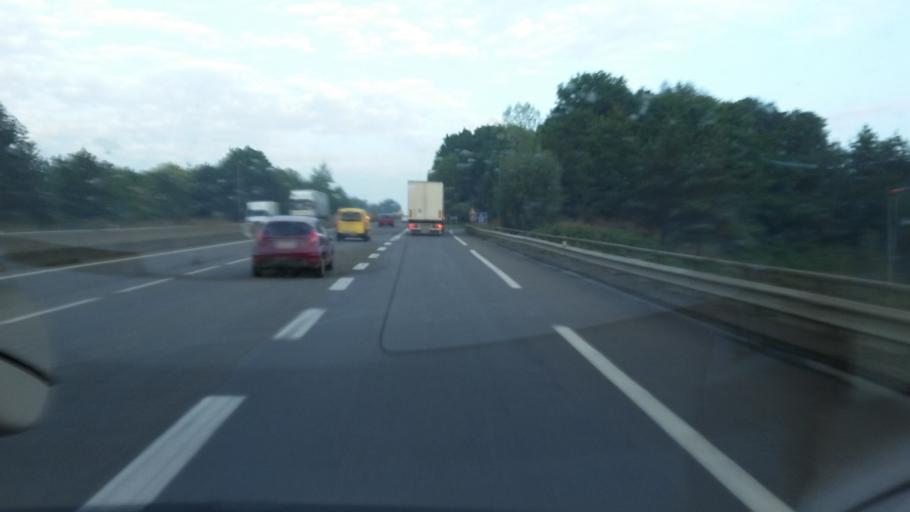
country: FR
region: Champagne-Ardenne
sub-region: Departement des Ardennes
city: La Francheville
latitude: 49.7349
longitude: 4.7215
